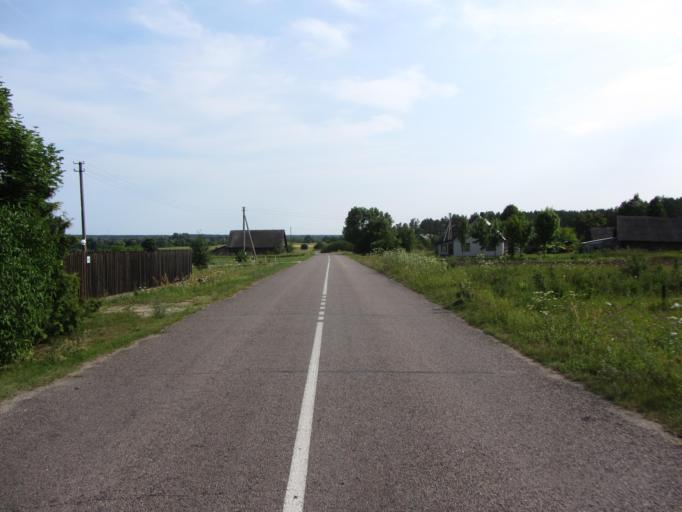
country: LT
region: Alytaus apskritis
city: Druskininkai
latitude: 53.9789
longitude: 23.9075
